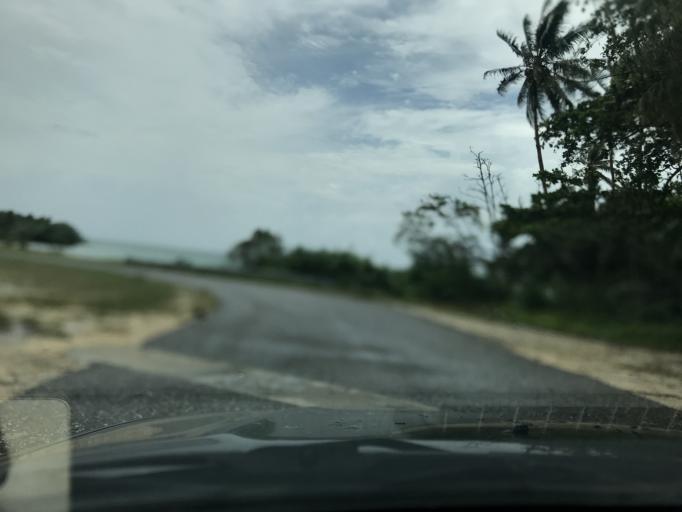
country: SB
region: Western Province
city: Gizo
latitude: -8.3281
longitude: 157.2520
